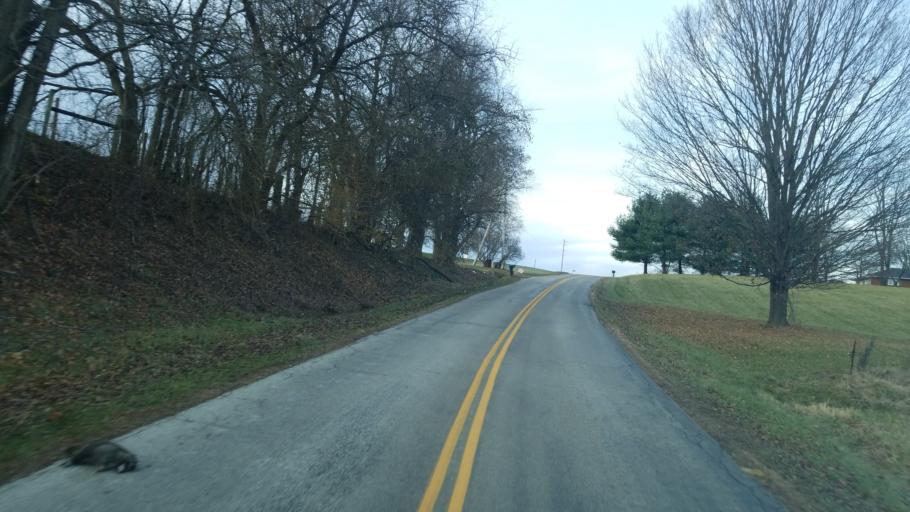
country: US
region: Ohio
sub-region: Sandusky County
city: Bellville
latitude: 40.6752
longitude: -82.4630
